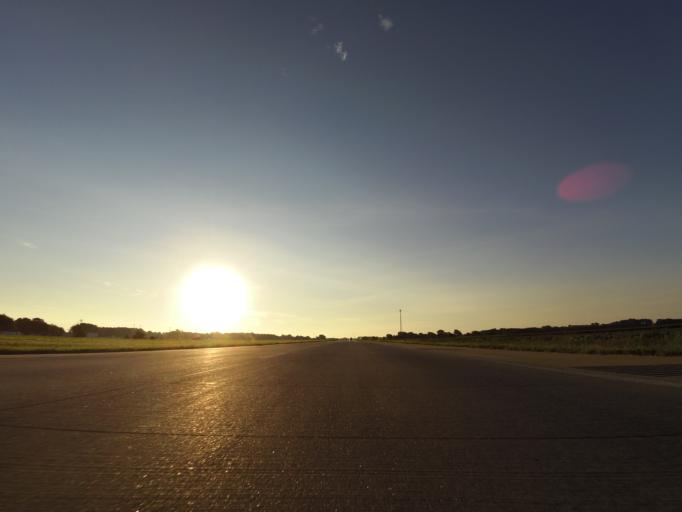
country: US
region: Kansas
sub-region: Reno County
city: Haven
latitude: 37.8953
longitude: -97.7819
